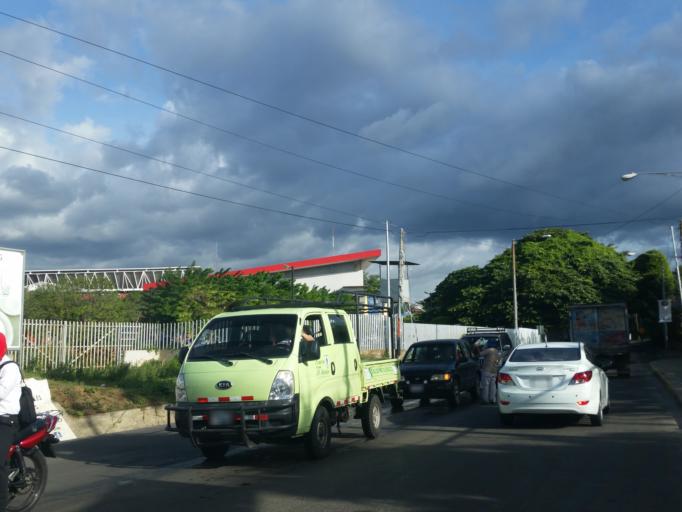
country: NI
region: Managua
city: Managua
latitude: 12.1050
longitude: -86.2508
